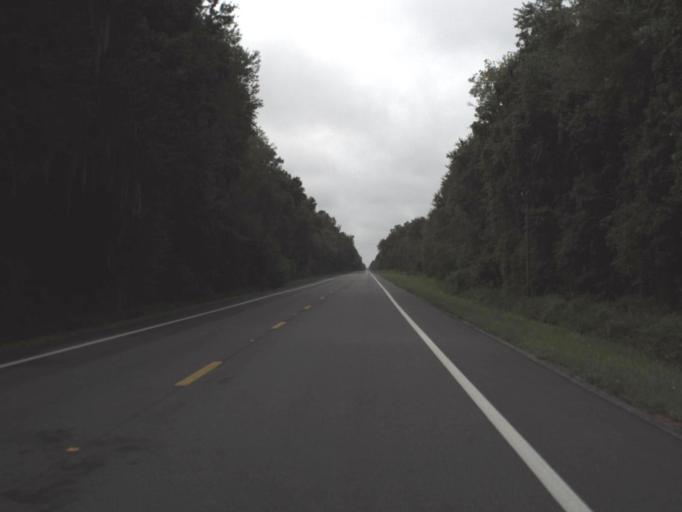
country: US
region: Florida
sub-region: Columbia County
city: Five Points
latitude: 30.4526
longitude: -82.6495
